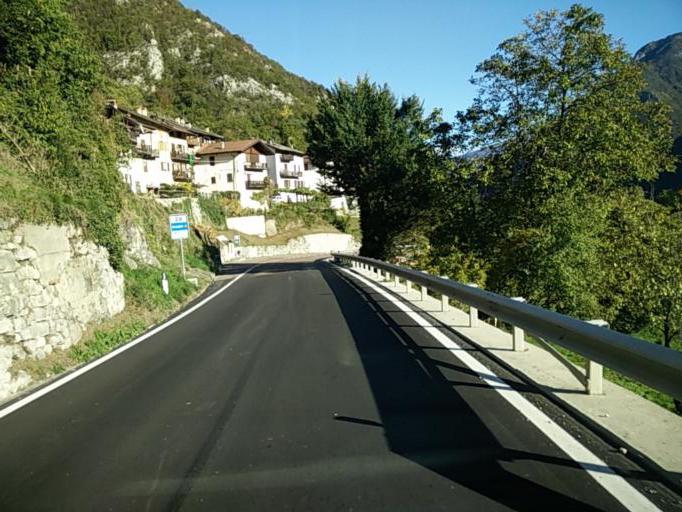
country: IT
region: Trentino-Alto Adige
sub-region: Provincia di Trento
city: Molina di Ledro
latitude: 45.8710
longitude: 10.7806
